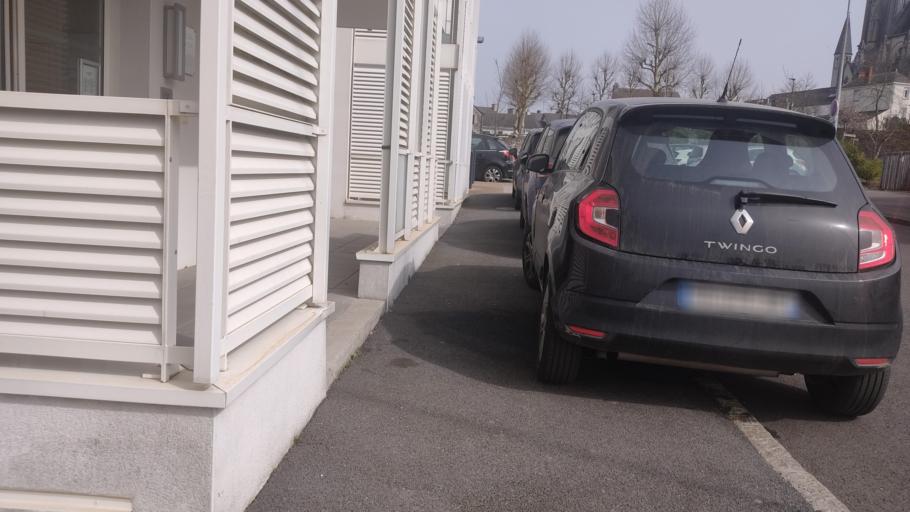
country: FR
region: Pays de la Loire
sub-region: Departement de la Loire-Atlantique
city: Carquefou
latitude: 47.2961
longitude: -1.4940
